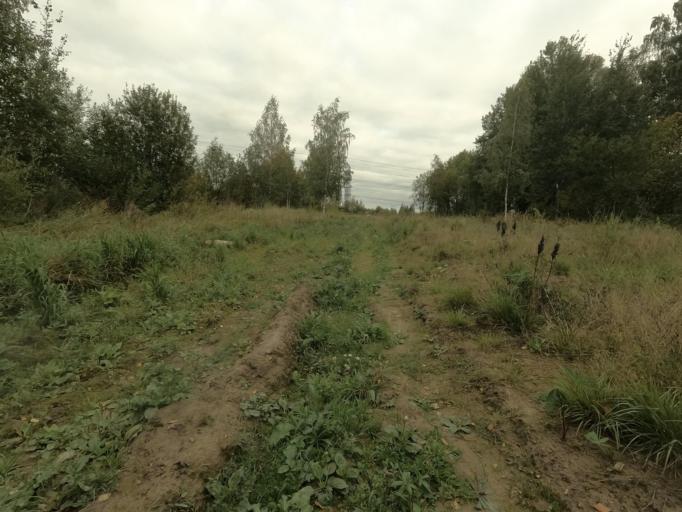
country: RU
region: St.-Petersburg
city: Metallostroy
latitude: 59.8158
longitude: 30.5447
